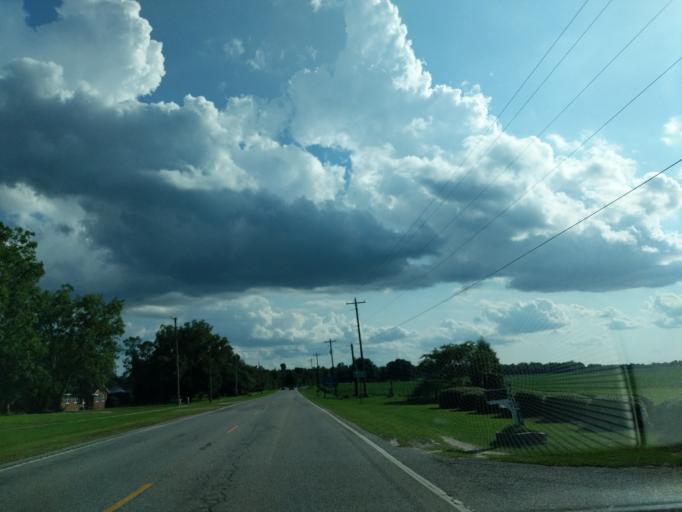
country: US
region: South Carolina
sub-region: Barnwell County
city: Williston
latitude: 33.4184
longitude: -81.4035
